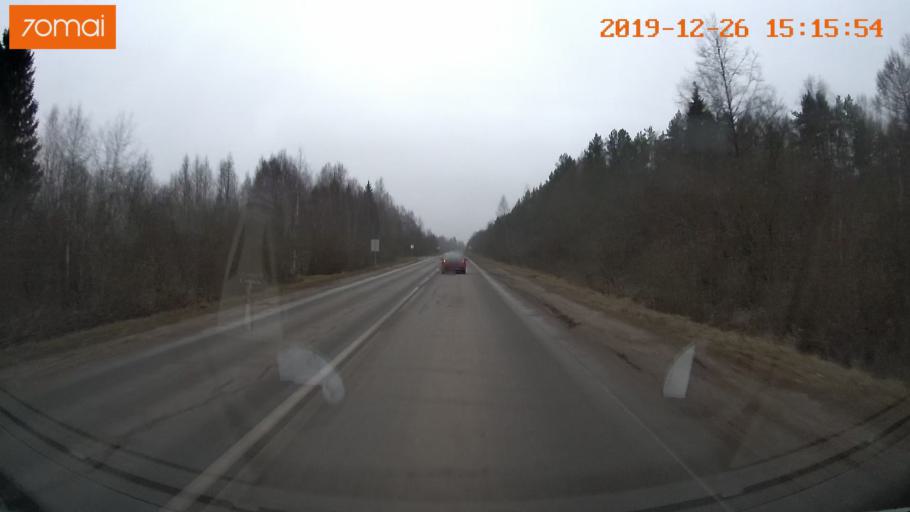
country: RU
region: Jaroslavl
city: Rybinsk
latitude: 58.0921
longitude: 38.8730
